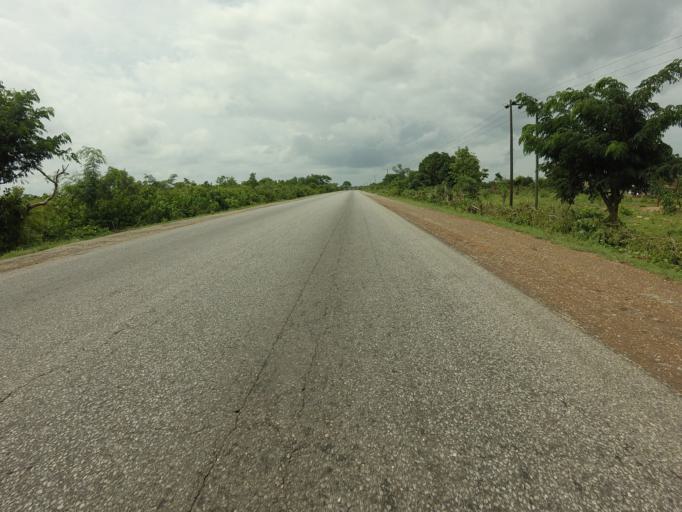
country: GH
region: Brong-Ahafo
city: Kintampo
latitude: 8.7448
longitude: -1.4637
